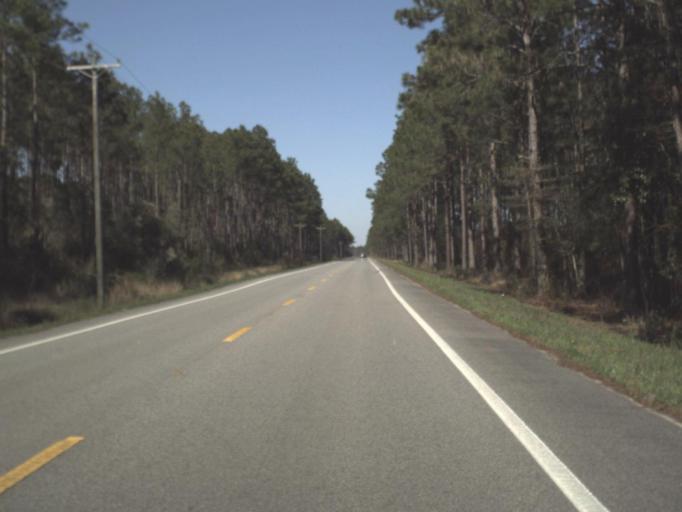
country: US
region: Florida
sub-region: Gulf County
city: Wewahitchka
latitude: 29.9588
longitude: -85.1768
